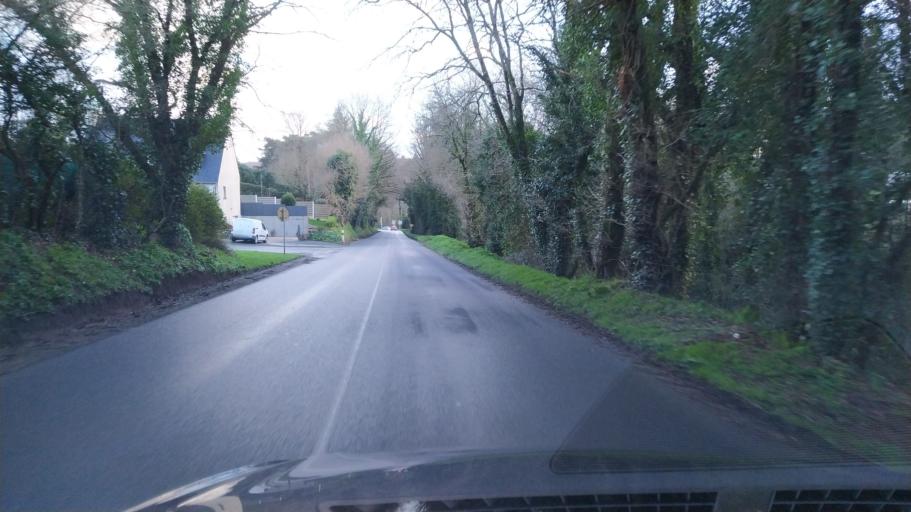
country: FR
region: Brittany
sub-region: Departement du Finistere
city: Landivisiau
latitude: 48.5014
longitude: -4.0946
